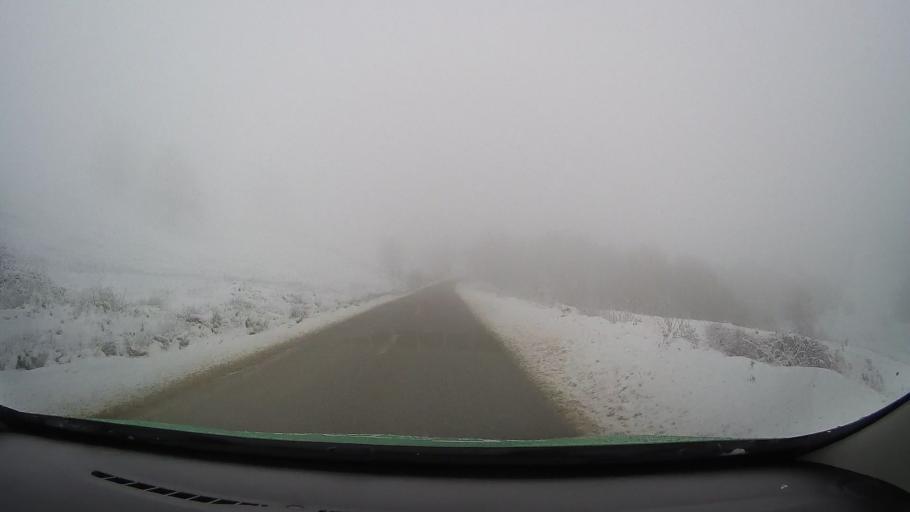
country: RO
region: Hunedoara
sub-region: Comuna Unirea
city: Unirea
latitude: 45.6638
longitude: 22.9136
